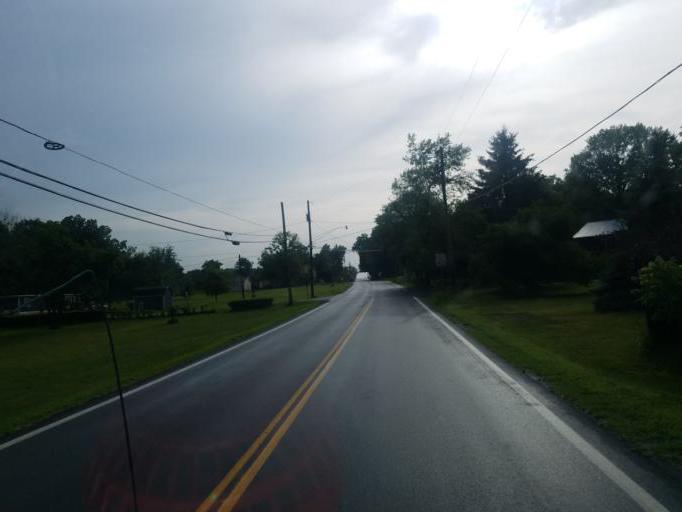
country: US
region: Ohio
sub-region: Wayne County
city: West Salem
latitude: 40.9260
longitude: -82.0533
